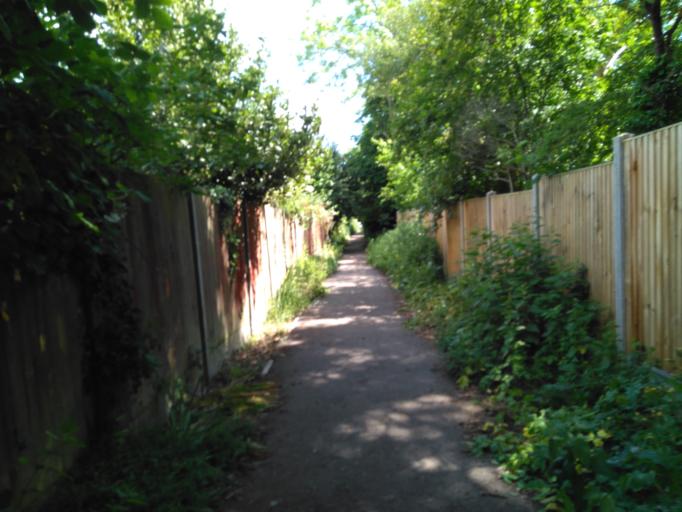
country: GB
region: England
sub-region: Kent
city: Whitstable
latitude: 51.3522
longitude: 1.0186
